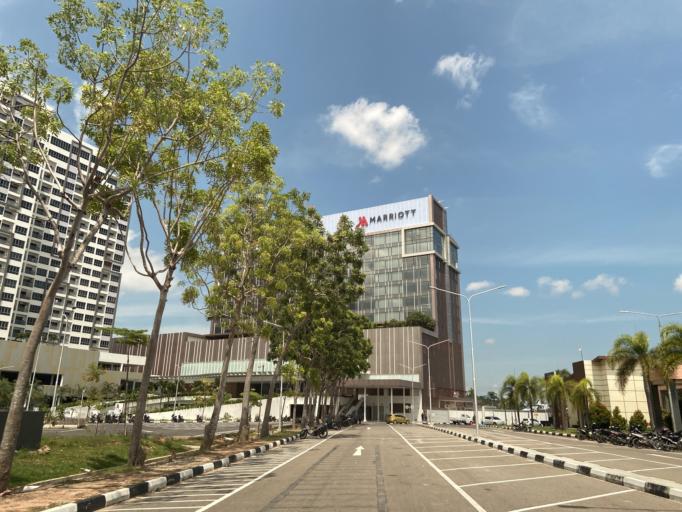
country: SG
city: Singapore
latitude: 1.1555
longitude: 103.9969
